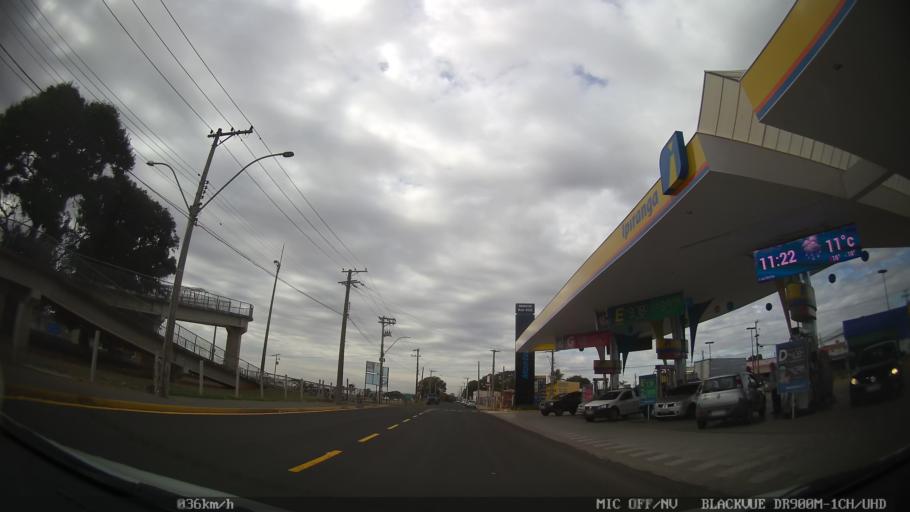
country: BR
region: Sao Paulo
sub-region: Sao Jose Do Rio Preto
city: Sao Jose do Rio Preto
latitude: -20.8111
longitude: -49.4921
